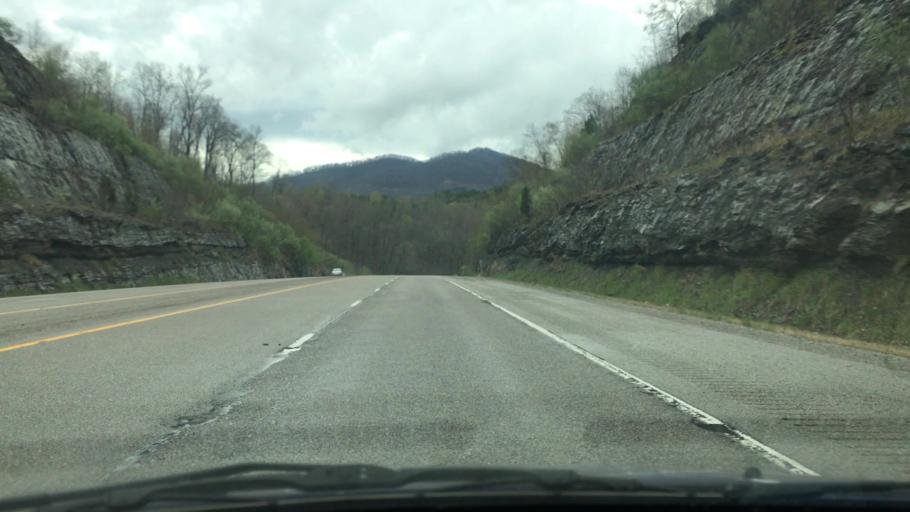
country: US
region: Kentucky
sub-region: Letcher County
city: Jenkins
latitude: 37.1853
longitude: -82.6361
